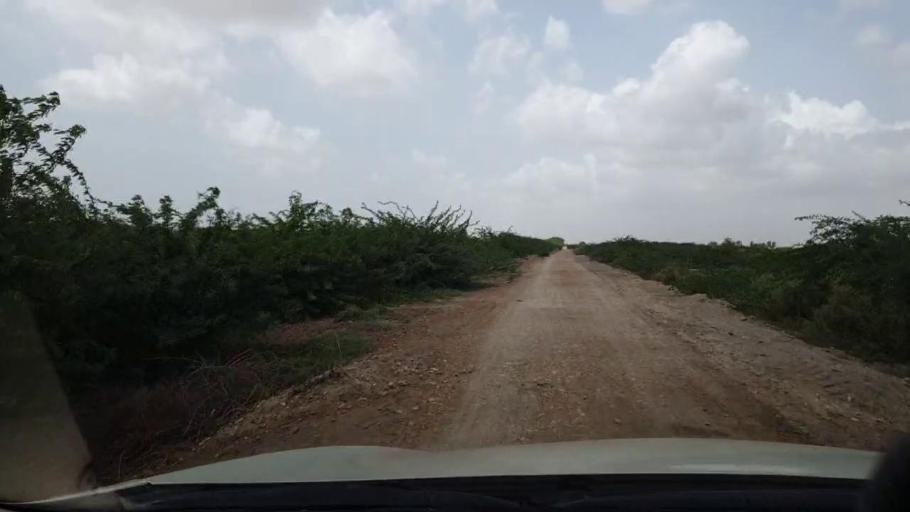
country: PK
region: Sindh
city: Kadhan
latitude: 24.3711
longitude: 68.8541
